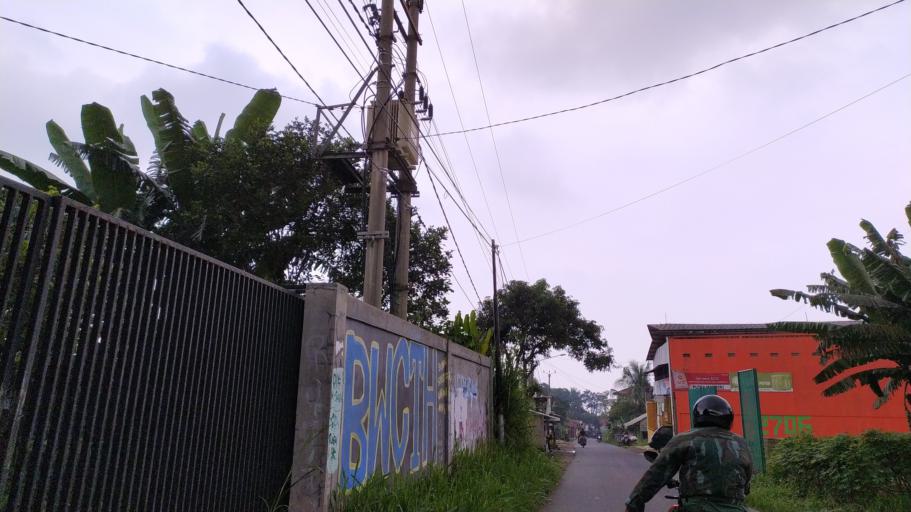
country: ID
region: West Java
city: Ciampea
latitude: -6.6158
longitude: 106.6950
